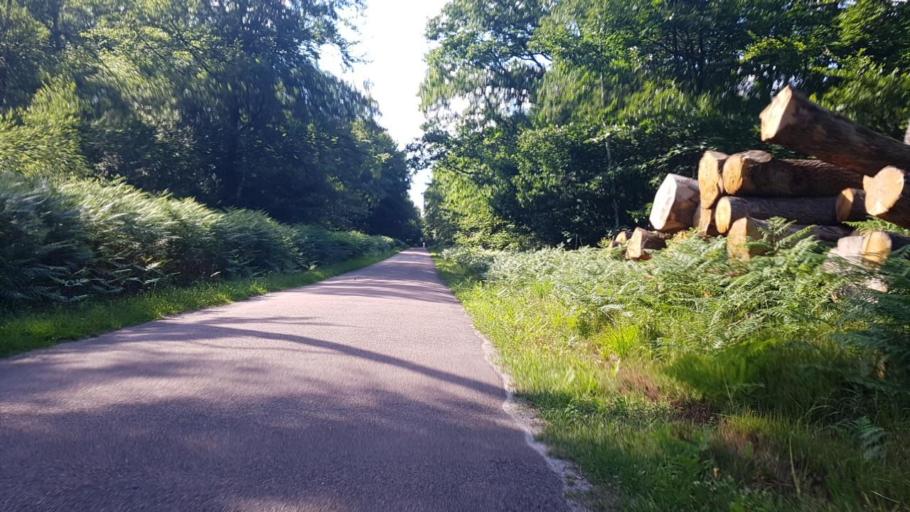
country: FR
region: Picardie
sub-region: Departement de l'Oise
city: Ver-sur-Launette
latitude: 49.1486
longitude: 2.6437
